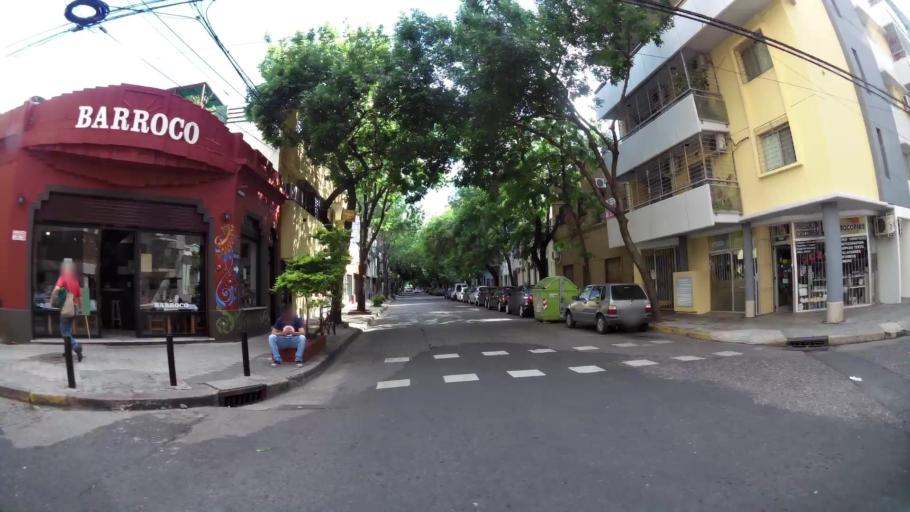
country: AR
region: Santa Fe
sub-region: Departamento de Rosario
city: Rosario
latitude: -32.9571
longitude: -60.6292
